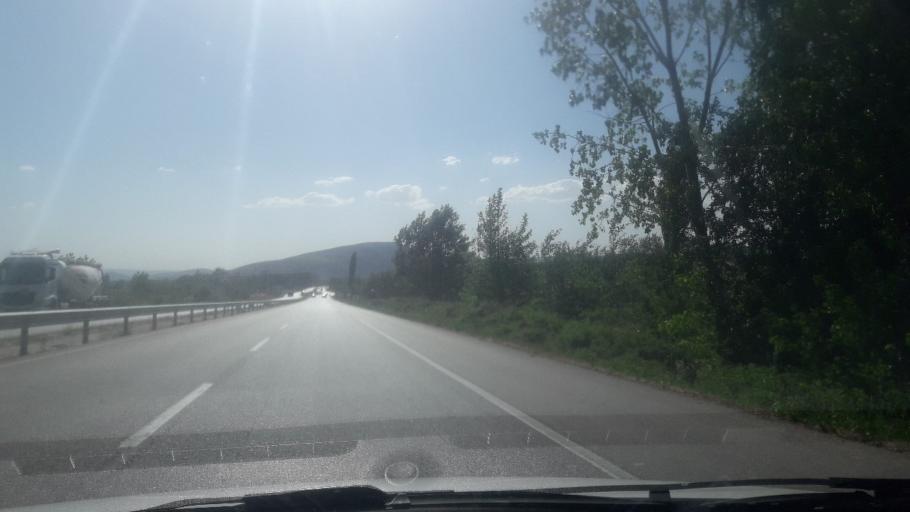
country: TR
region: Tokat
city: Dokmetepe
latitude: 40.3212
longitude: 36.1940
